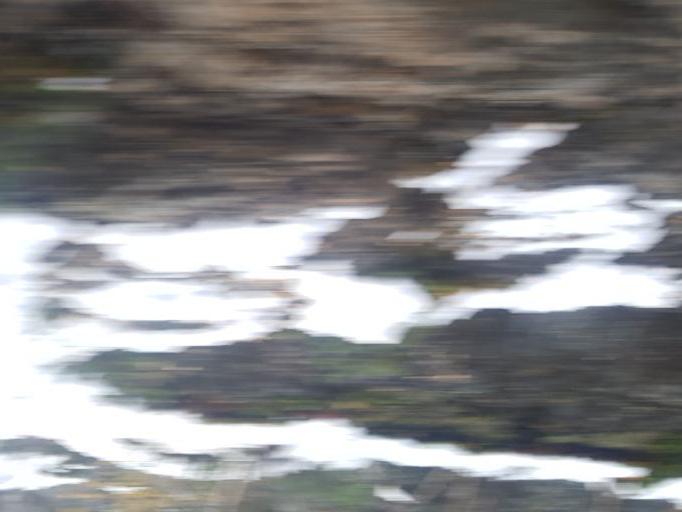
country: NO
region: Sor-Trondelag
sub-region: Oppdal
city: Oppdal
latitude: 62.4048
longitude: 9.6307
